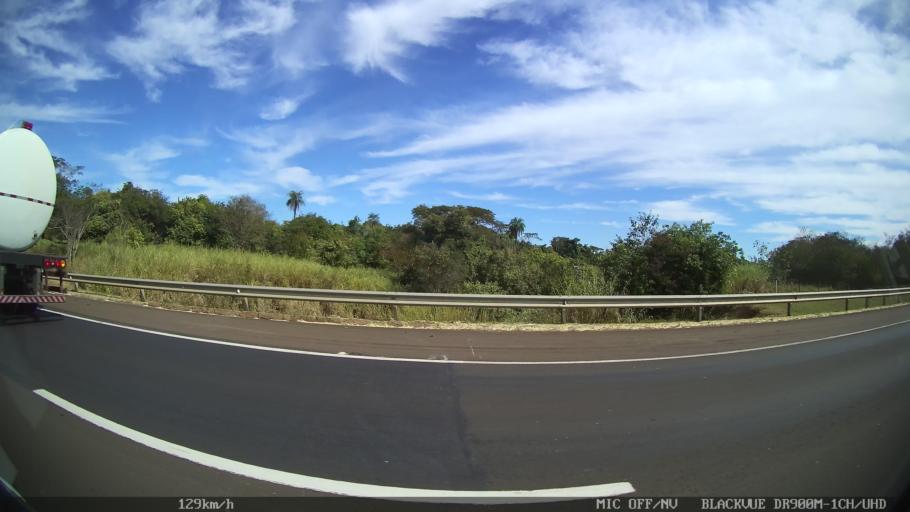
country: BR
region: Sao Paulo
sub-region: Matao
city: Matao
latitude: -21.6149
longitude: -48.4194
